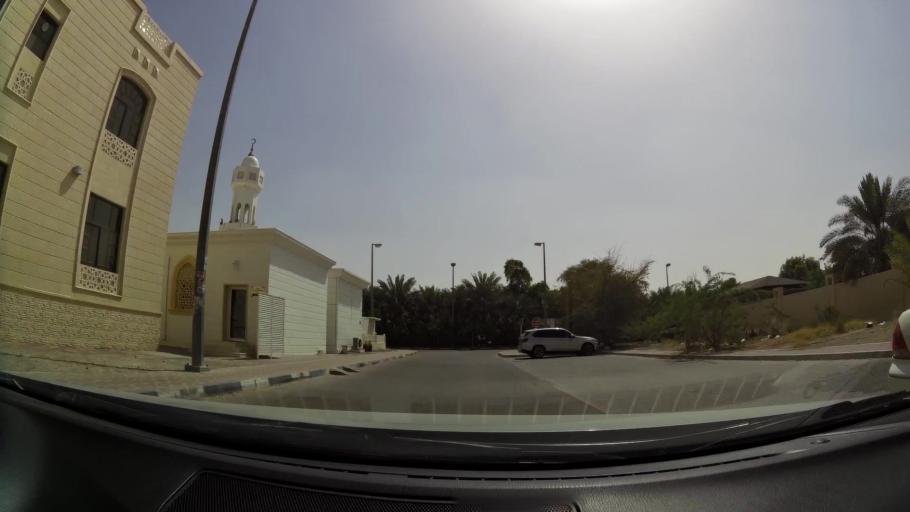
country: AE
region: Abu Dhabi
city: Al Ain
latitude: 24.2223
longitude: 55.6884
